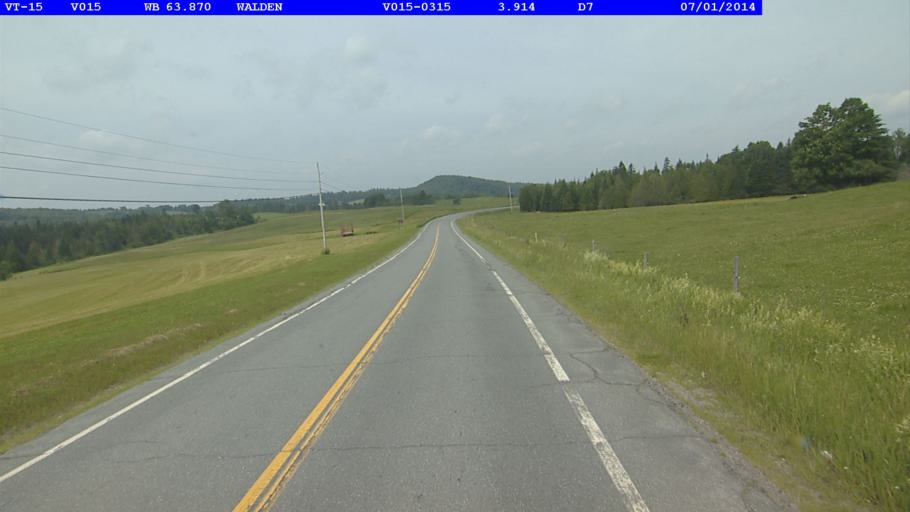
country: US
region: Vermont
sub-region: Caledonia County
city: Hardwick
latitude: 44.4490
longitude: -72.2489
